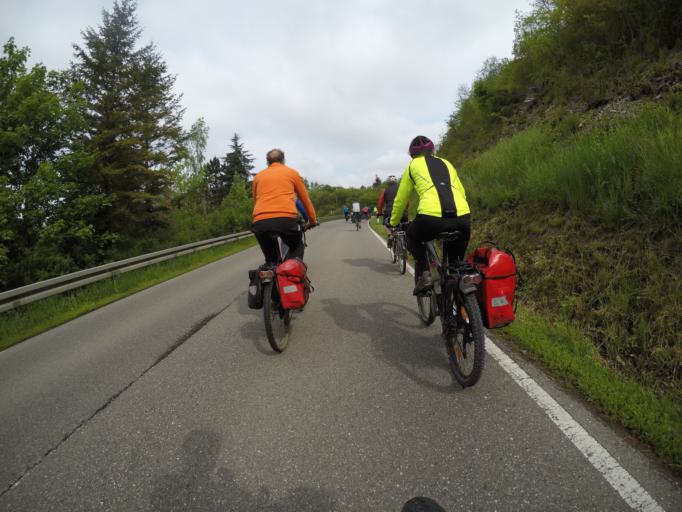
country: DE
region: Baden-Wuerttemberg
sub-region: Regierungsbezirk Stuttgart
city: Weil der Stadt
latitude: 48.7680
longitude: 8.8988
